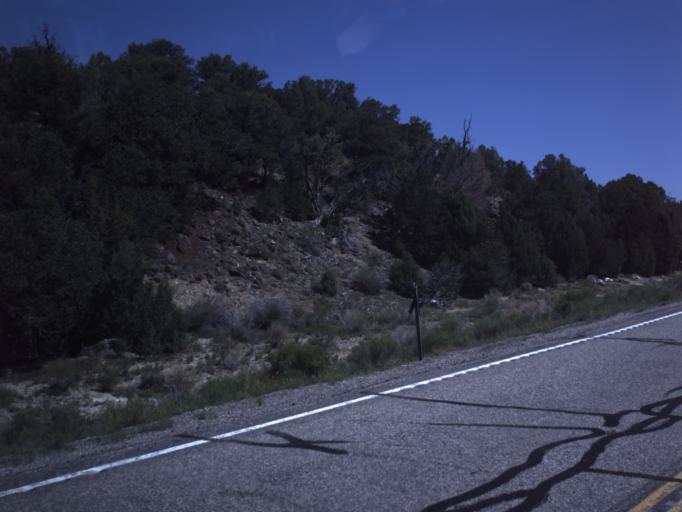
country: US
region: Utah
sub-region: Wayne County
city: Loa
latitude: 38.6780
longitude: -111.4006
